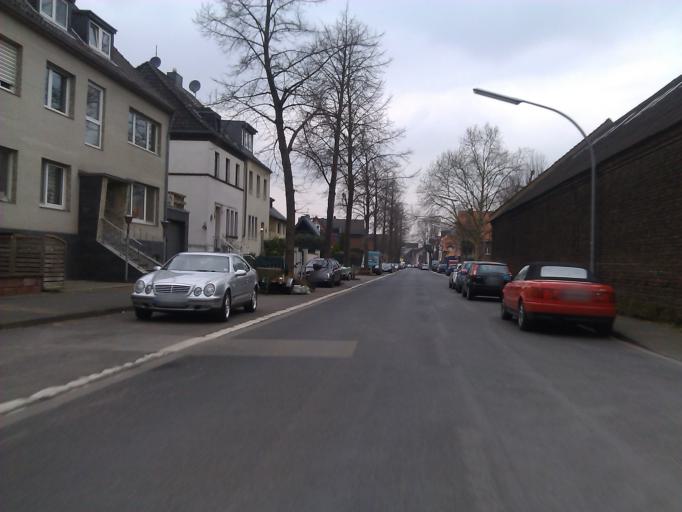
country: DE
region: North Rhine-Westphalia
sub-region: Regierungsbezirk Koln
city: Leverkusen
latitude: 51.0217
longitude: 6.9612
